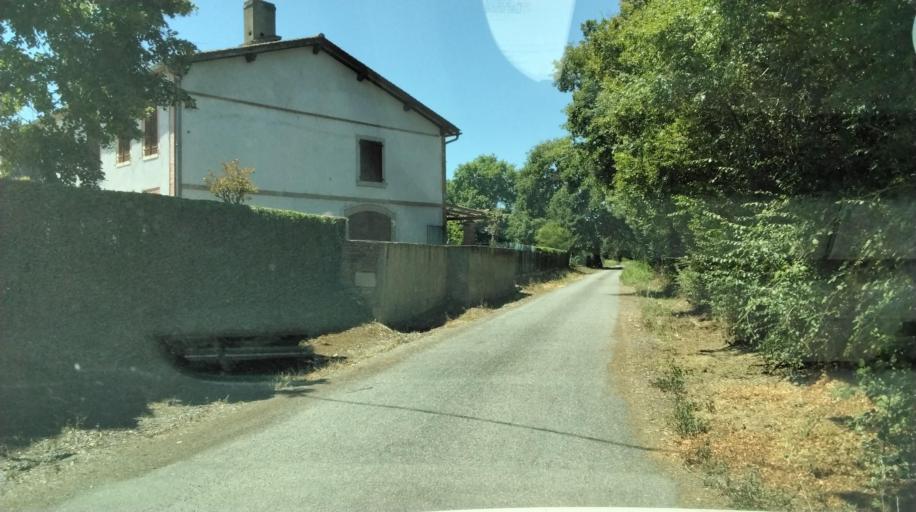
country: FR
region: Midi-Pyrenees
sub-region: Departement de la Haute-Garonne
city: Rieux-Volvestre
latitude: 43.2750
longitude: 1.1367
